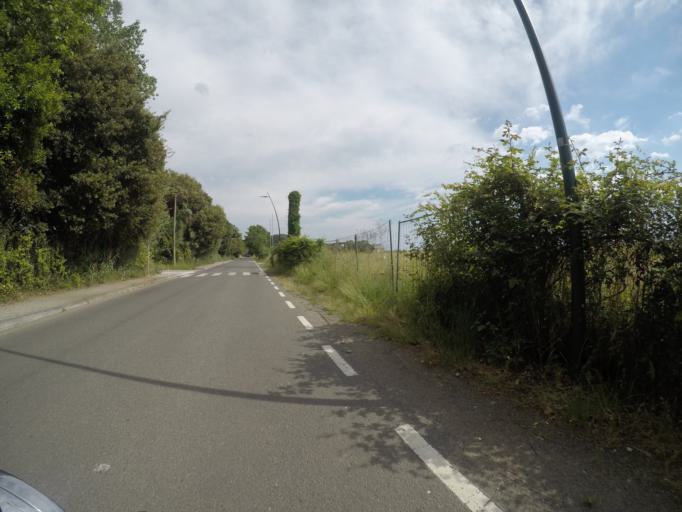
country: IT
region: Tuscany
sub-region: Provincia di Massa-Carrara
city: Capanne-Prato-Cinquale
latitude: 43.9761
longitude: 10.1489
